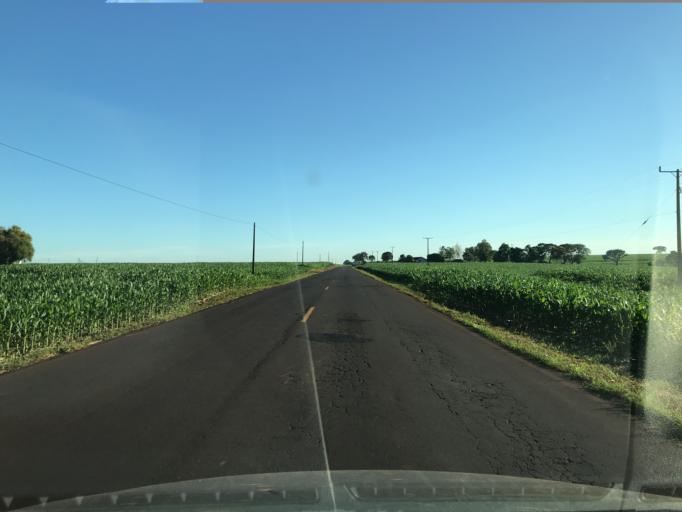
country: BR
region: Parana
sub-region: Palotina
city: Palotina
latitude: -24.1215
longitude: -53.8489
